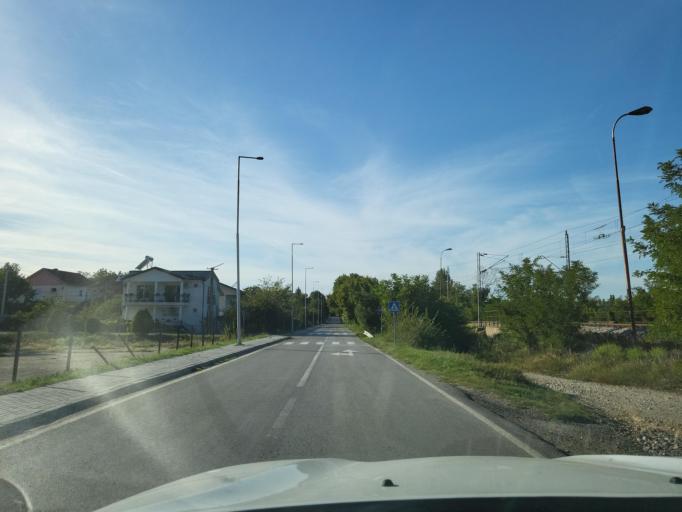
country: MK
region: Demir Kapija
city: Demir Kapija
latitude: 41.4132
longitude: 22.2401
